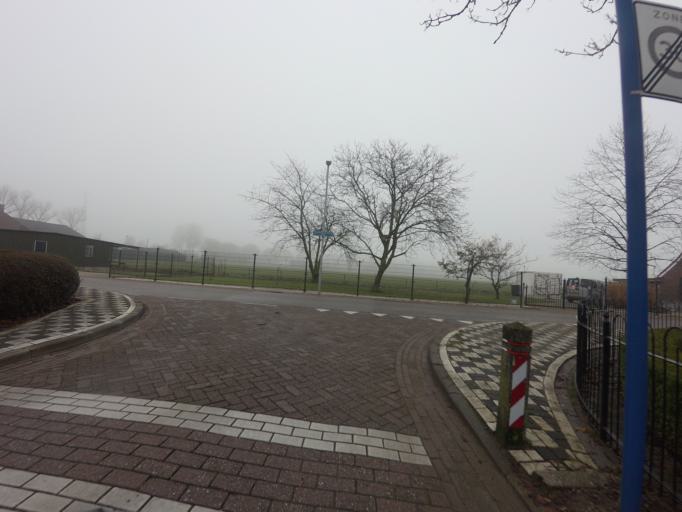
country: NL
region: Gelderland
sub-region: Gemeente Zaltbommel
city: Nederhemert
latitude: 51.7670
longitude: 5.1681
